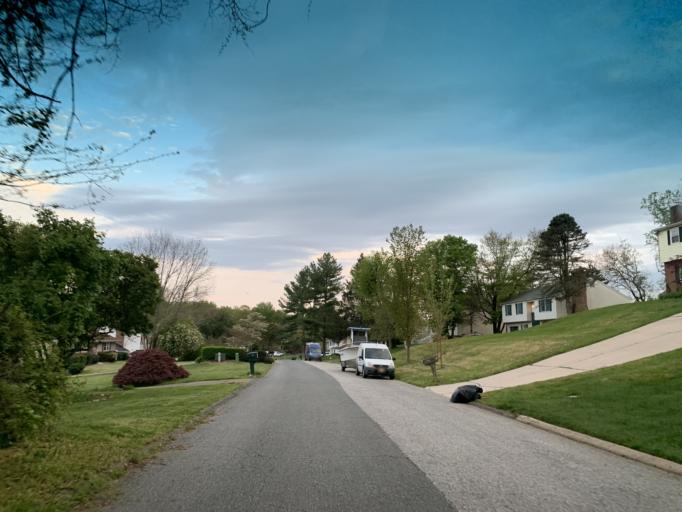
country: US
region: Maryland
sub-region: Harford County
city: Bel Air South
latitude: 39.5038
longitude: -76.3452
